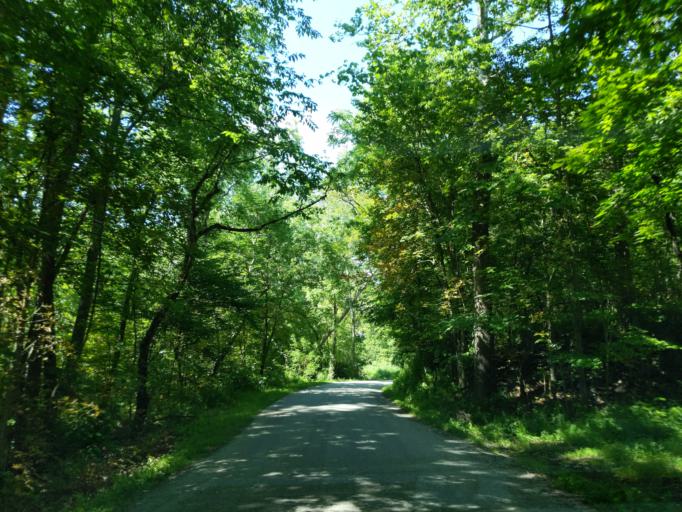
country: US
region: Indiana
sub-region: Ripley County
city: Osgood
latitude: 39.2011
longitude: -85.4163
